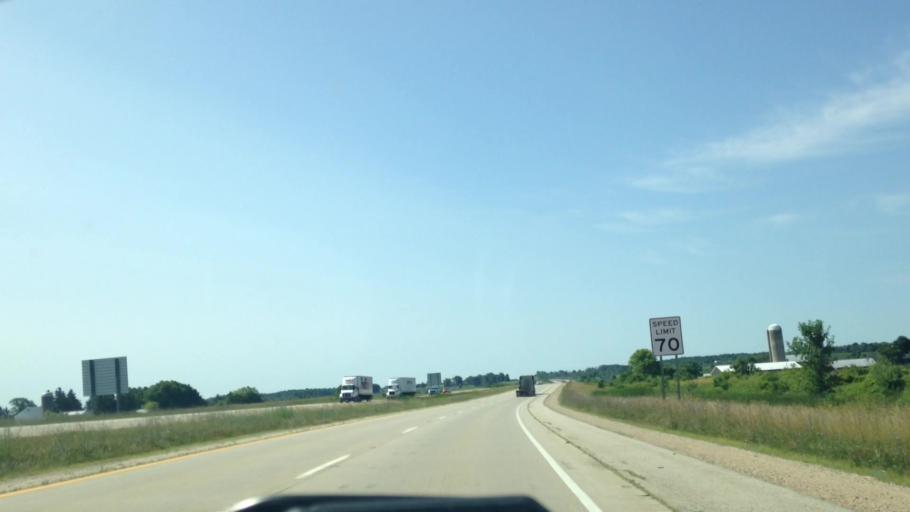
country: US
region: Wisconsin
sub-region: Washington County
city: Jackson
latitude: 43.3149
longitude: -88.1844
